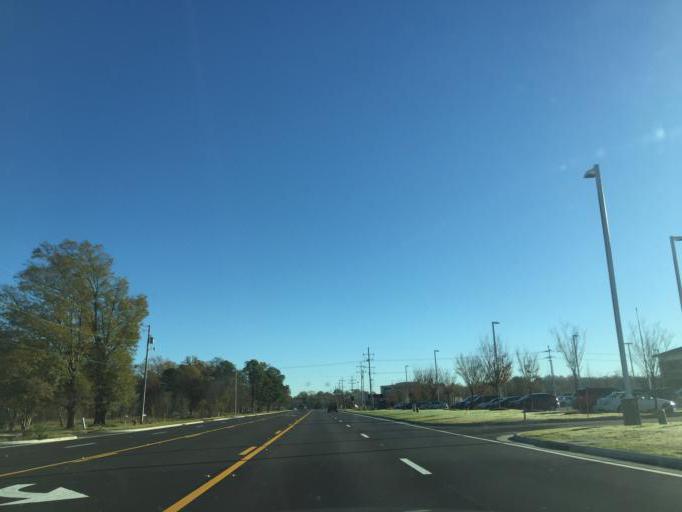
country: US
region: Mississippi
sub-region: Rankin County
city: Flowood
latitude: 32.3228
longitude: -90.1112
